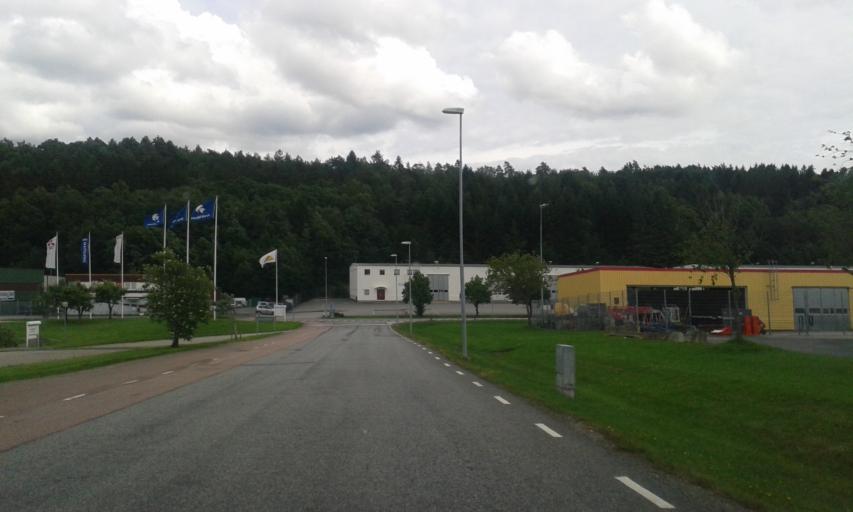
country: SE
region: Vaestra Goetaland
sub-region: Kungalvs Kommun
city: Kungalv
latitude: 57.8775
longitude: 11.9449
